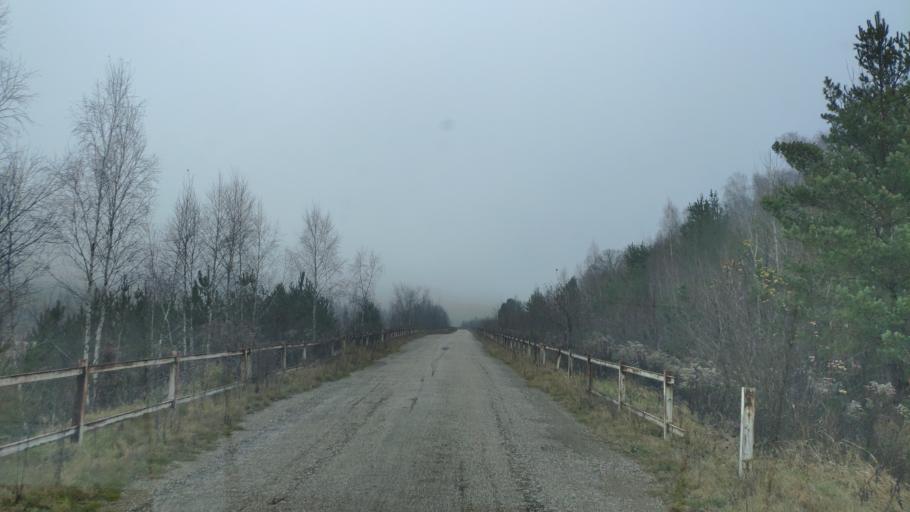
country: SK
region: Banskobystricky
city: Revuca
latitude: 48.6432
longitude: 20.2443
